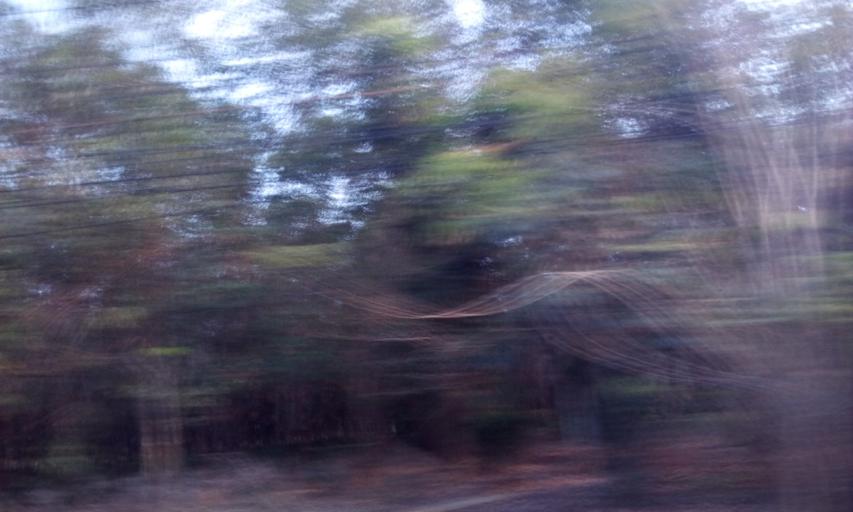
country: TH
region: Trat
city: Laem Ngop
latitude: 12.2619
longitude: 102.2937
